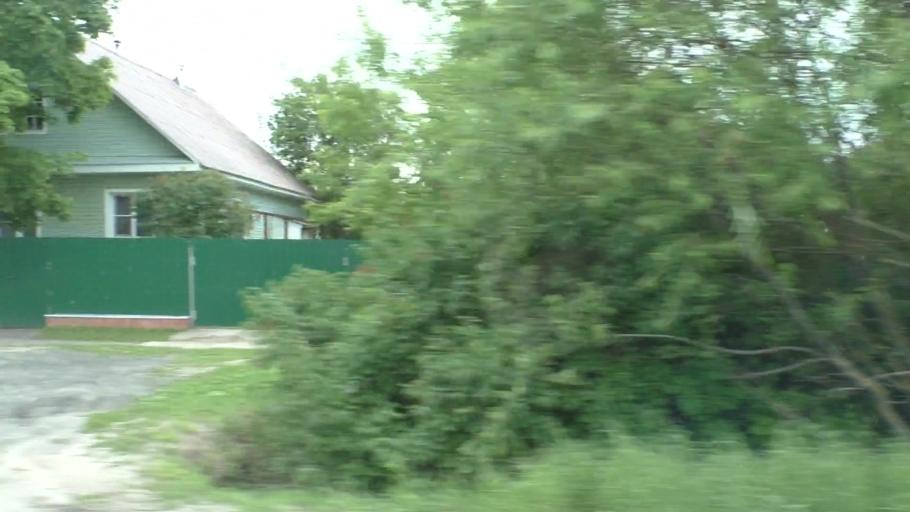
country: RU
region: Moskovskaya
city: Il'inskiy Pogost
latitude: 55.5018
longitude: 38.7966
